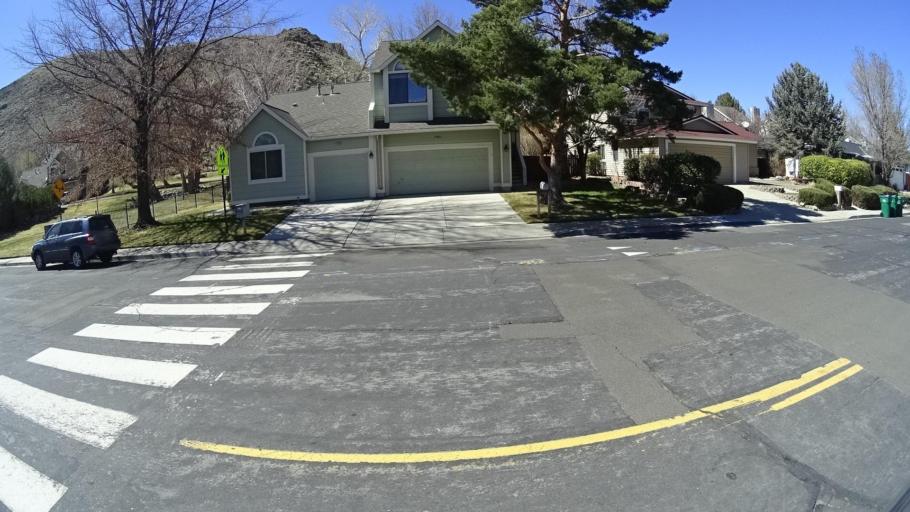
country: US
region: Nevada
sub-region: Washoe County
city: Sparks
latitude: 39.4765
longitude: -119.7540
